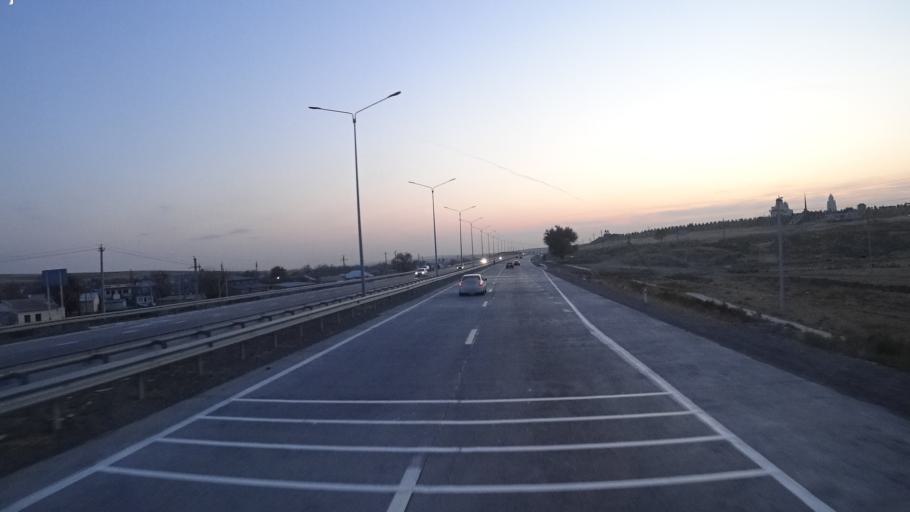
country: KZ
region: Ongtustik Qazaqstan
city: Qazyqurt
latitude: 41.8787
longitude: 69.4343
